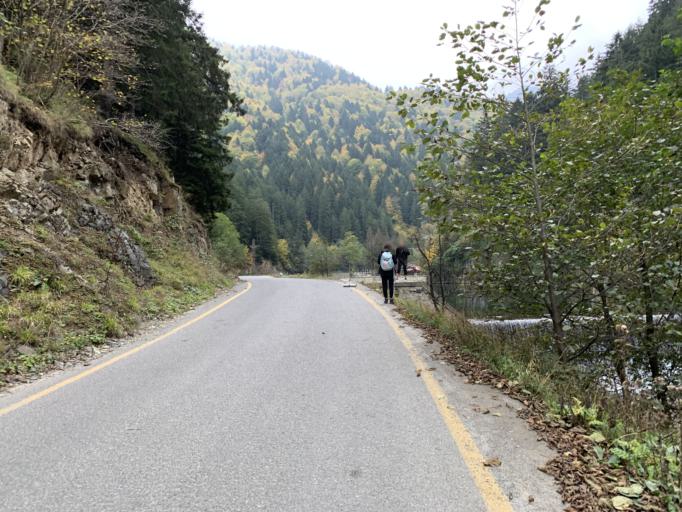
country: TR
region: Trabzon
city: Uzungol
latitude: 40.5998
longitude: 40.3177
